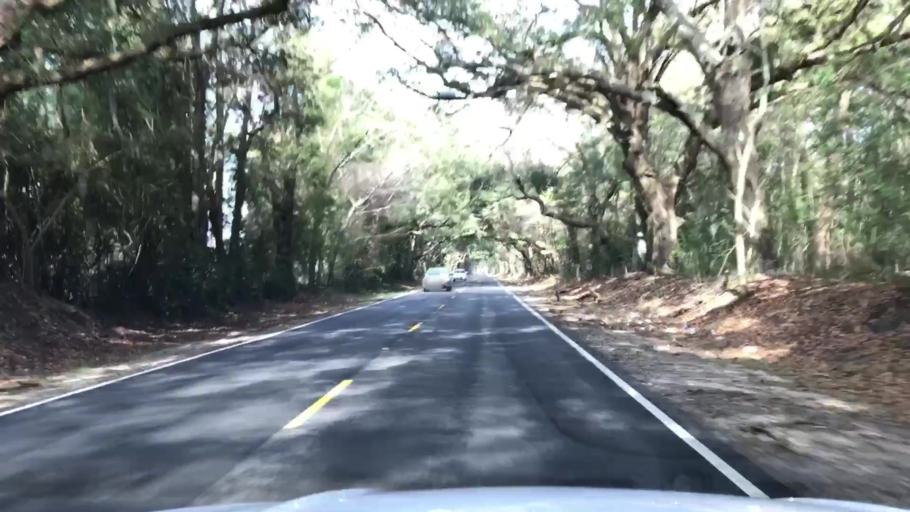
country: US
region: South Carolina
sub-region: Charleston County
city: Folly Beach
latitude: 32.7081
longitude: -80.0171
